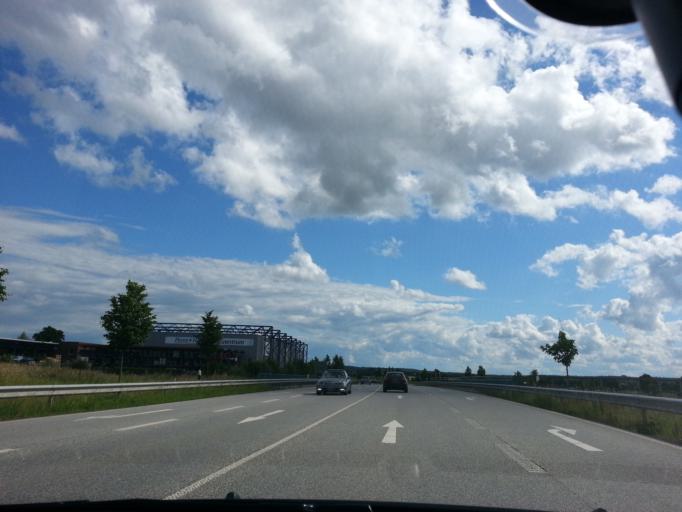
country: DE
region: Schleswig-Holstein
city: Einhaus
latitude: 53.7021
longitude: 10.7318
